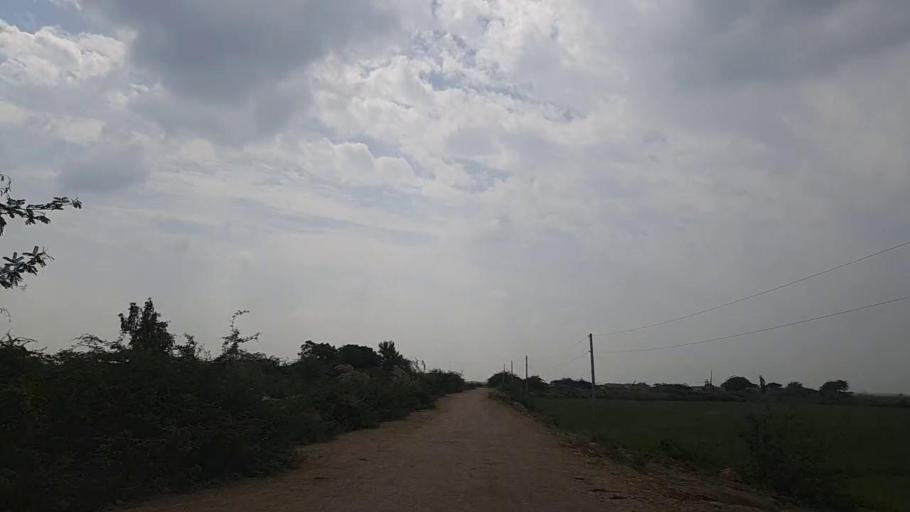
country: PK
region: Sindh
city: Mirpur Batoro
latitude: 24.6216
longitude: 68.1370
